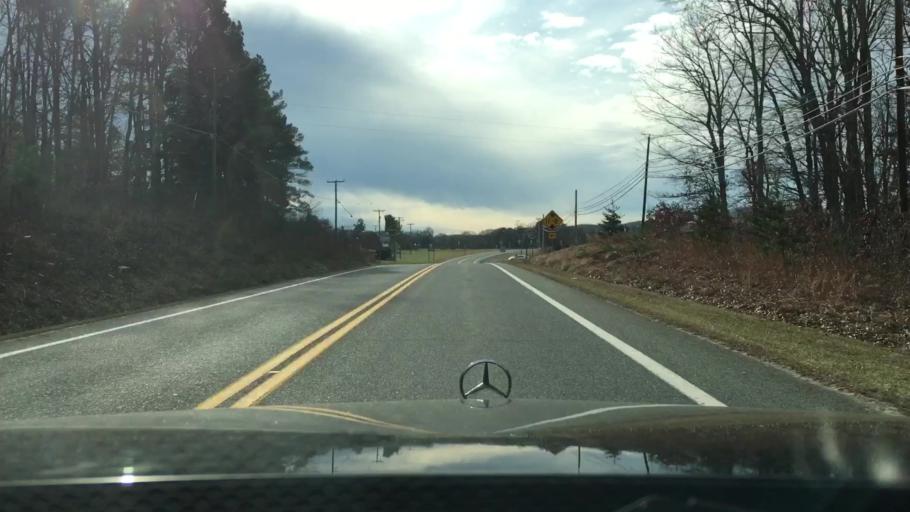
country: US
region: Virginia
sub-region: Pittsylvania County
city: Motley
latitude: 37.0821
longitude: -79.3306
